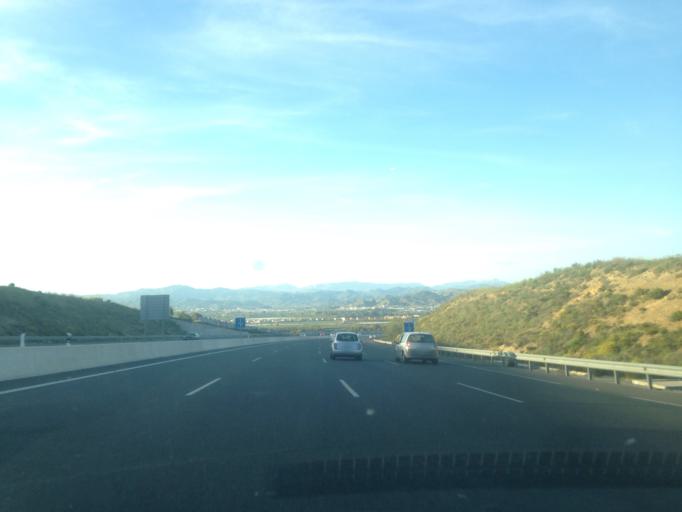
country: ES
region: Andalusia
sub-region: Provincia de Malaga
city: Alhaurin de la Torre
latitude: 36.6662
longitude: -4.5290
